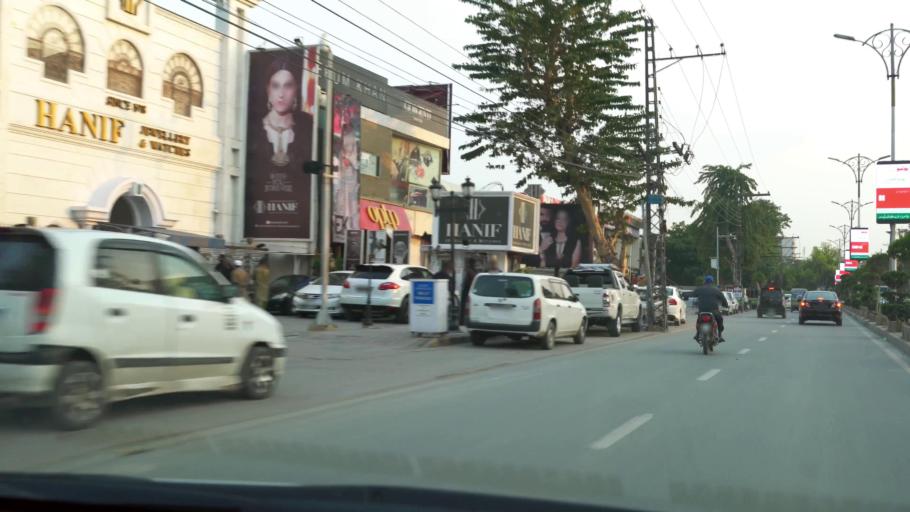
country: PK
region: Punjab
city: Lahore
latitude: 31.5098
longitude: 74.3504
